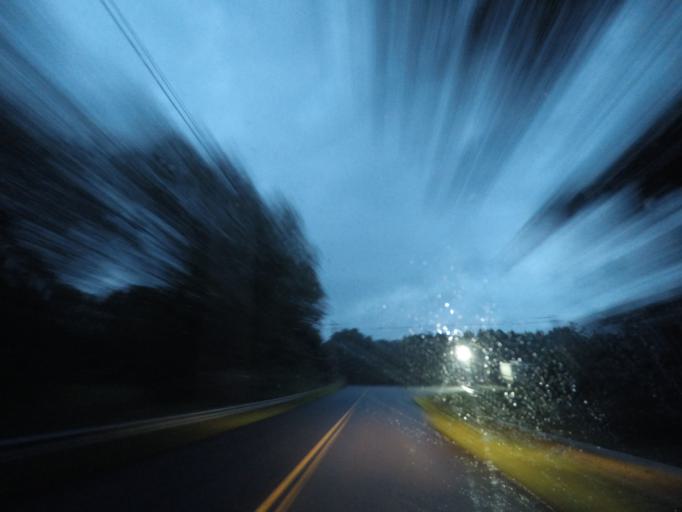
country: US
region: Massachusetts
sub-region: Worcester County
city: Sturbridge
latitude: 42.0699
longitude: -72.0986
